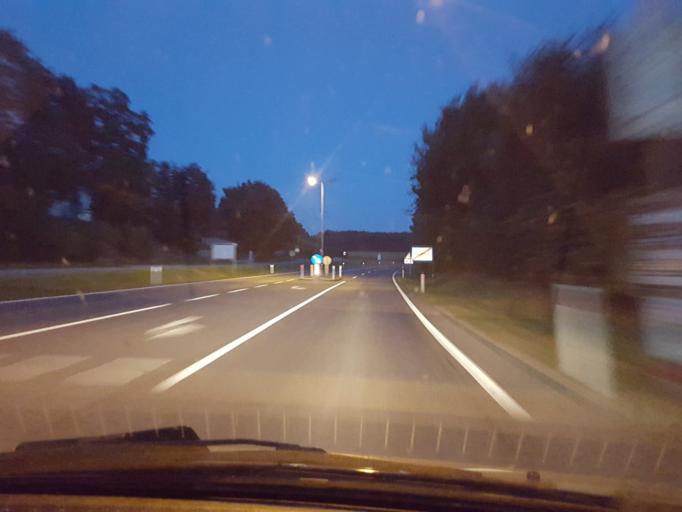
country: AT
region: Lower Austria
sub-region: Politischer Bezirk Scheibbs
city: Wieselburg
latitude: 48.1561
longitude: 15.1149
